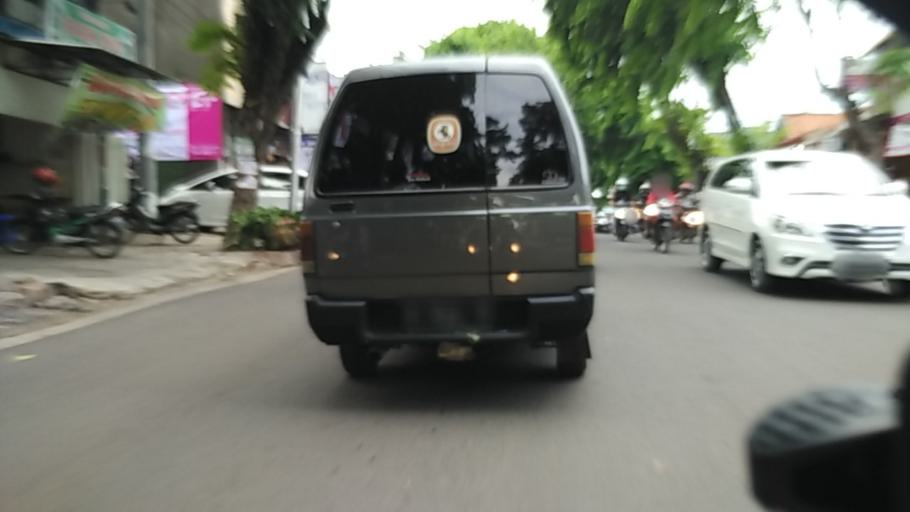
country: ID
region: Central Java
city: Semarang
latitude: -7.0495
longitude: 110.4215
